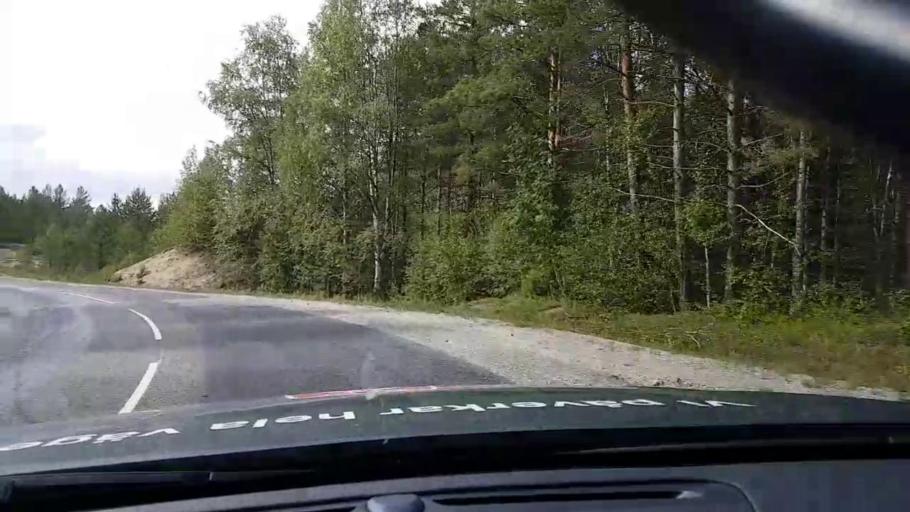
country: SE
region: Vaesterbotten
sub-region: Asele Kommun
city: Asele
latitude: 63.7945
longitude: 17.5757
